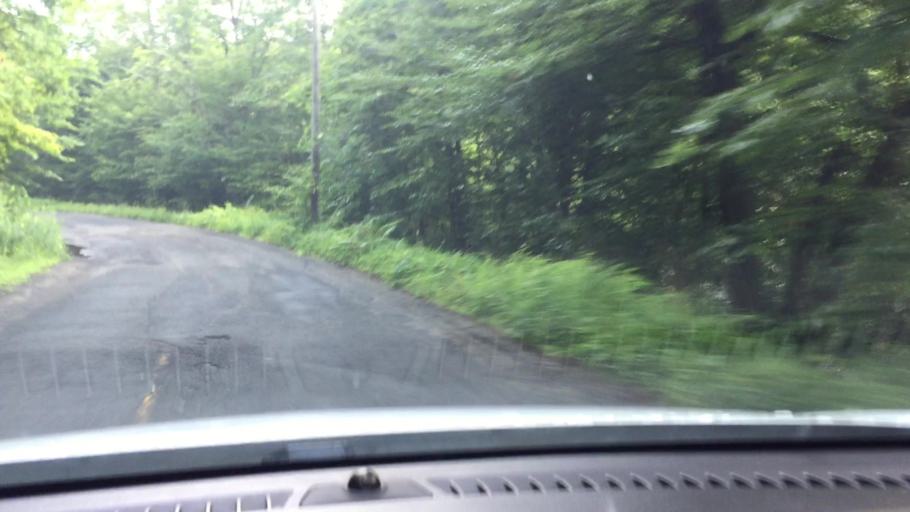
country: US
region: Massachusetts
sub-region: Hampshire County
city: Chesterfield
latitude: 42.3109
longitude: -72.9177
